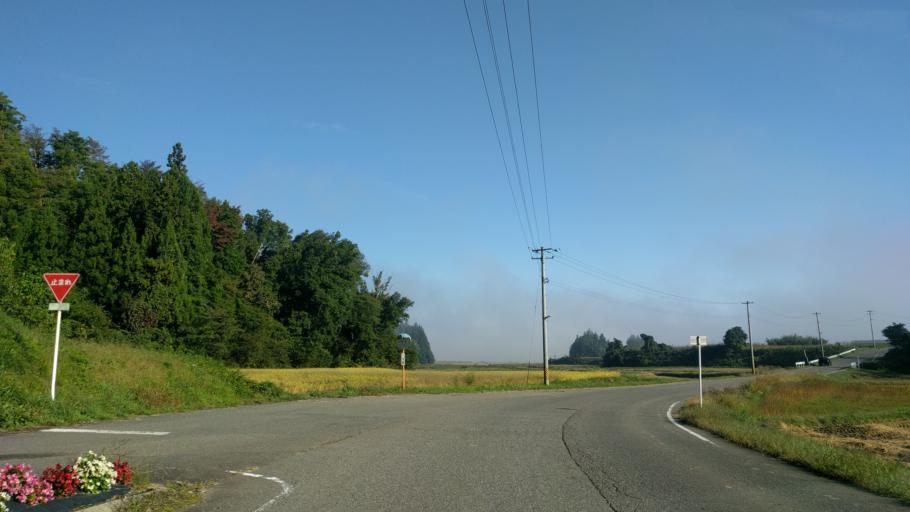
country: JP
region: Fukushima
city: Kitakata
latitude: 37.5211
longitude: 139.7980
